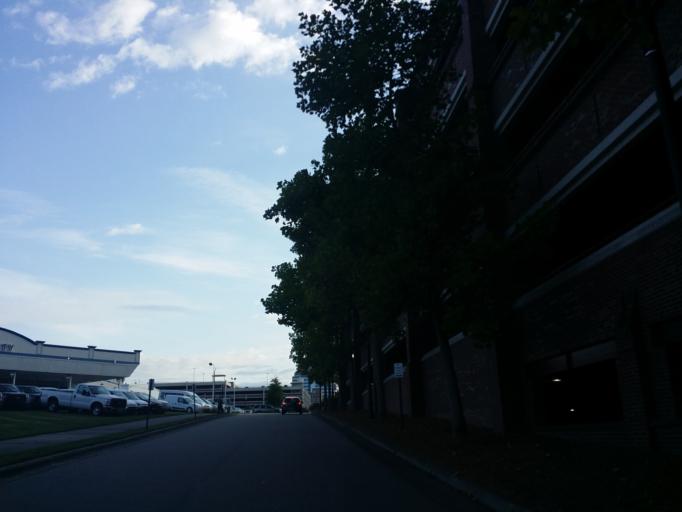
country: US
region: North Carolina
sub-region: Durham County
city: Durham
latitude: 35.9922
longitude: -78.9065
